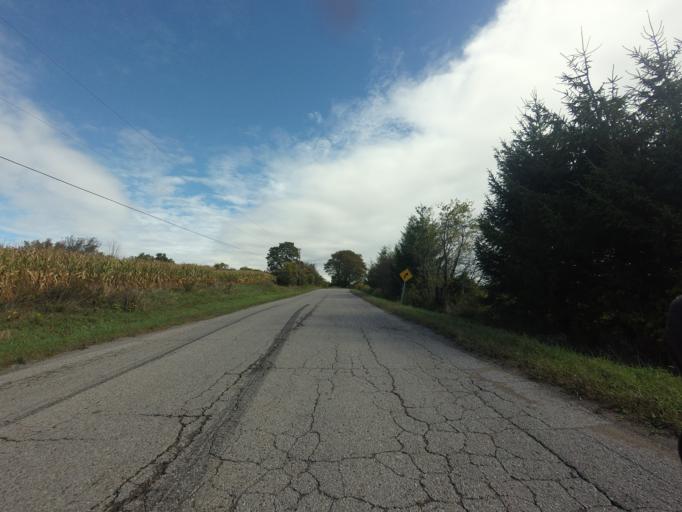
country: CA
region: Ontario
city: Cobourg
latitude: 43.9418
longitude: -78.3279
